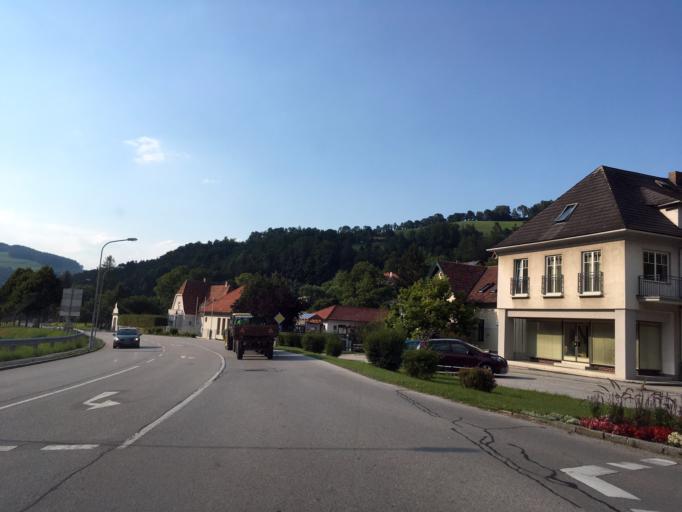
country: AT
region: Lower Austria
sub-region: Politischer Bezirk Neunkirchen
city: Edlitz
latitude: 47.5988
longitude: 16.1394
